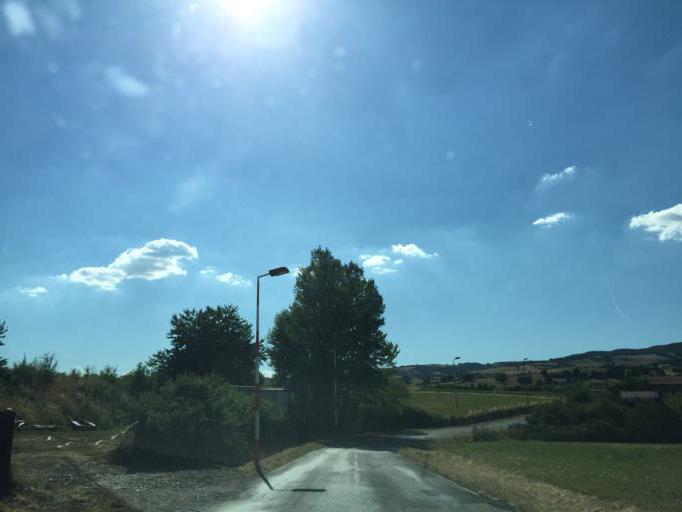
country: FR
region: Rhone-Alpes
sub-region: Departement de la Loire
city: La Grand-Croix
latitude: 45.4926
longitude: 4.5351
